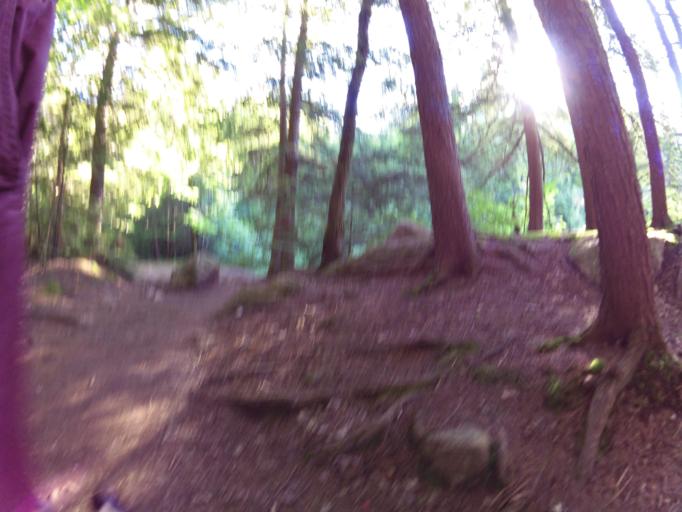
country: CA
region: Quebec
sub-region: Outaouais
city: Wakefield
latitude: 45.5834
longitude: -75.9814
